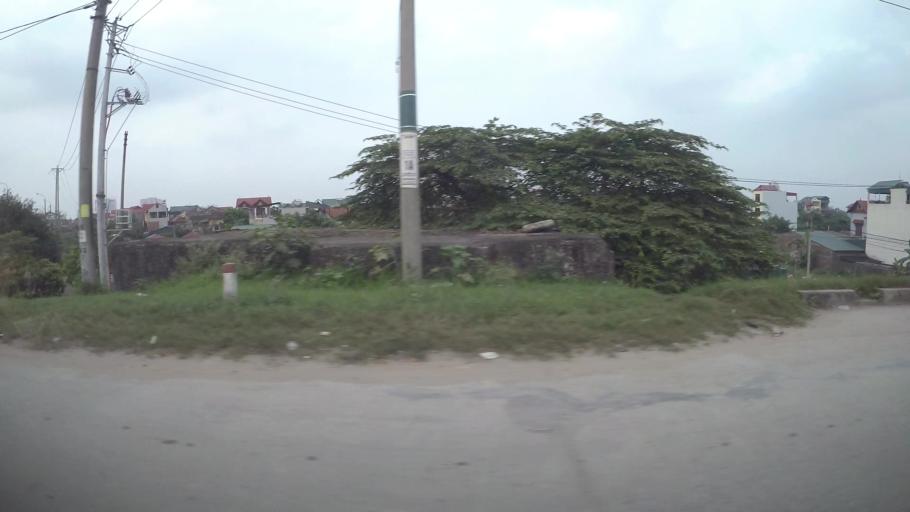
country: VN
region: Ha Noi
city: Trau Quy
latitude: 21.0050
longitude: 105.9085
